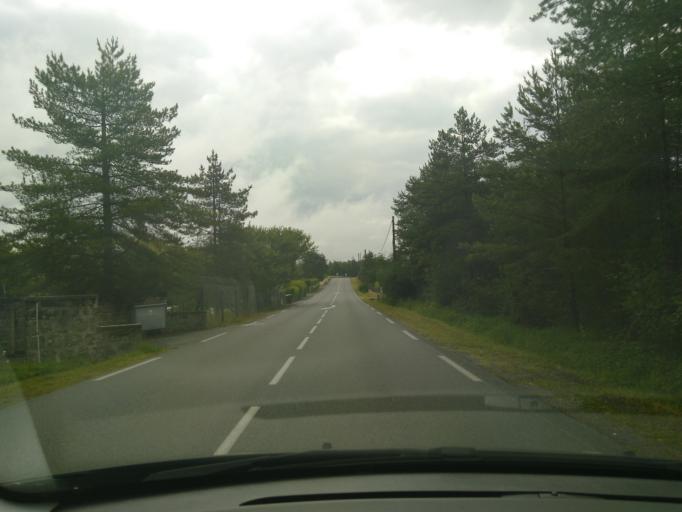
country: FR
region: Limousin
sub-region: Departement de la Correze
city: Cosnac
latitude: 45.1027
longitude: 1.5620
